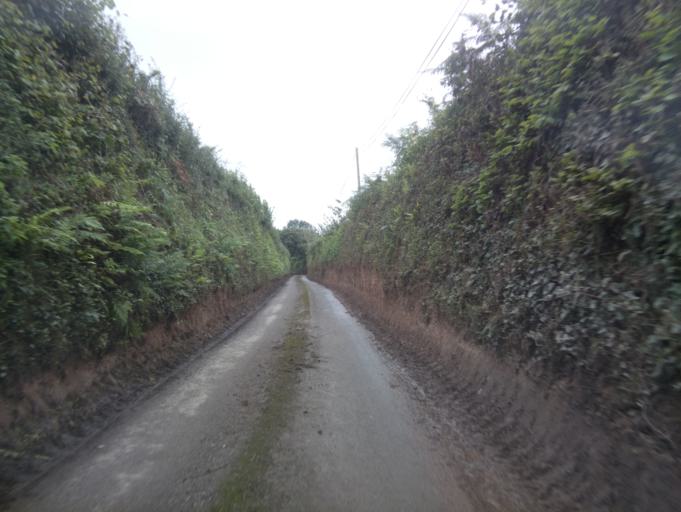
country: GB
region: England
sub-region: Devon
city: Kingsbridge
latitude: 50.2948
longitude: -3.7172
